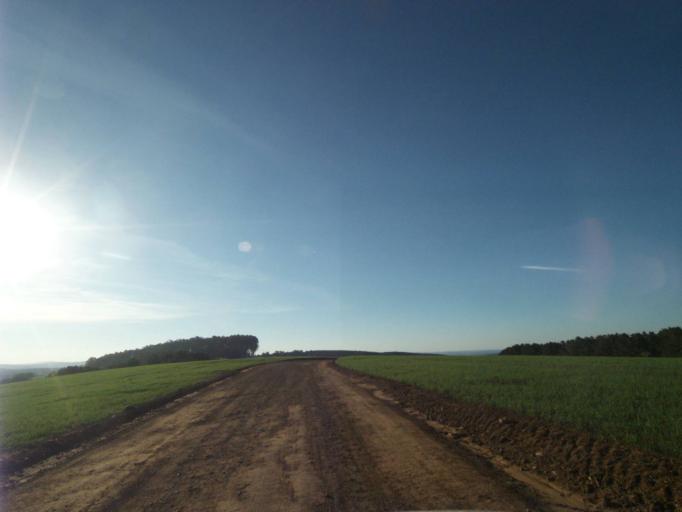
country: BR
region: Parana
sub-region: Telemaco Borba
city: Telemaco Borba
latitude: -24.4665
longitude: -50.5962
